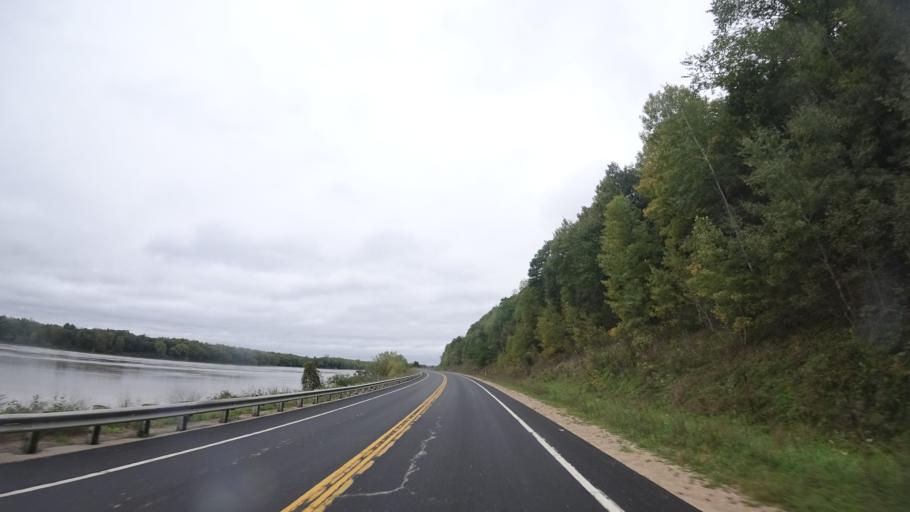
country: US
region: Wisconsin
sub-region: Grant County
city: Boscobel
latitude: 43.1753
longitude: -90.6905
